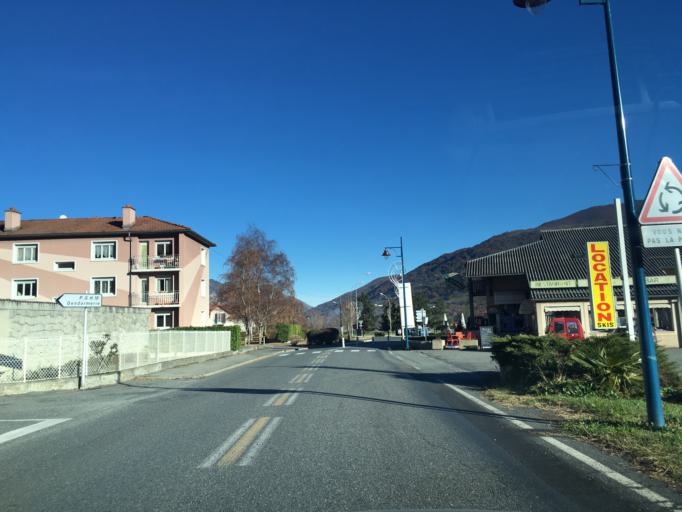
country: FR
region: Midi-Pyrenees
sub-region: Departement des Hautes-Pyrenees
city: Pierrefitte-Nestalas
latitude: 42.9653
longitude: -0.0740
